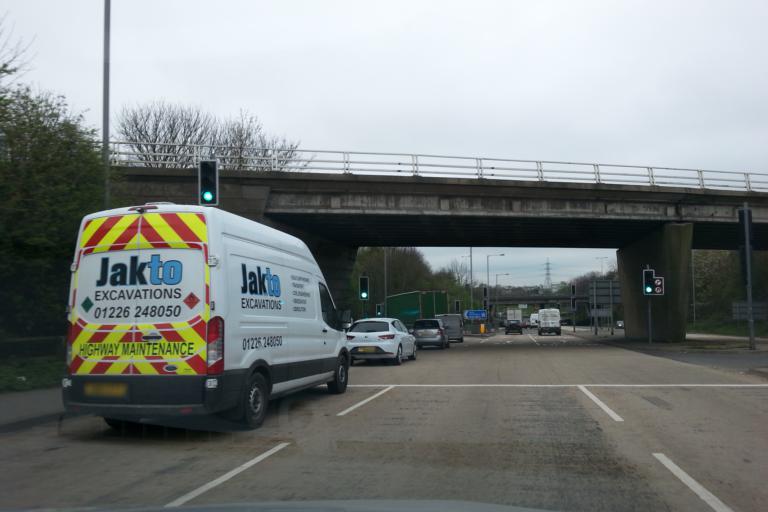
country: GB
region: England
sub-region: City and Borough of Leeds
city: Gildersome
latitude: 53.7488
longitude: -1.6353
